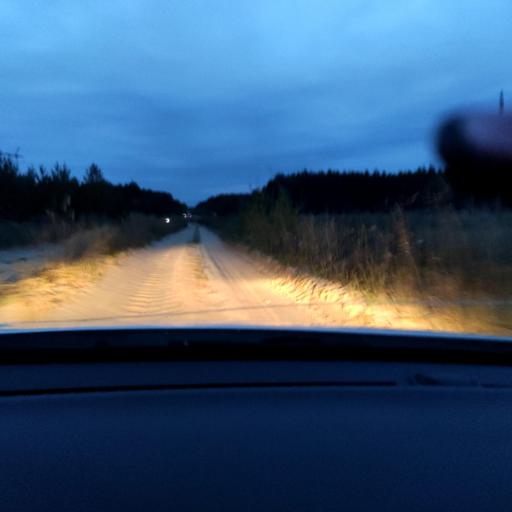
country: RU
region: Mariy-El
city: Volzhsk
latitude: 55.8894
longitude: 48.3979
